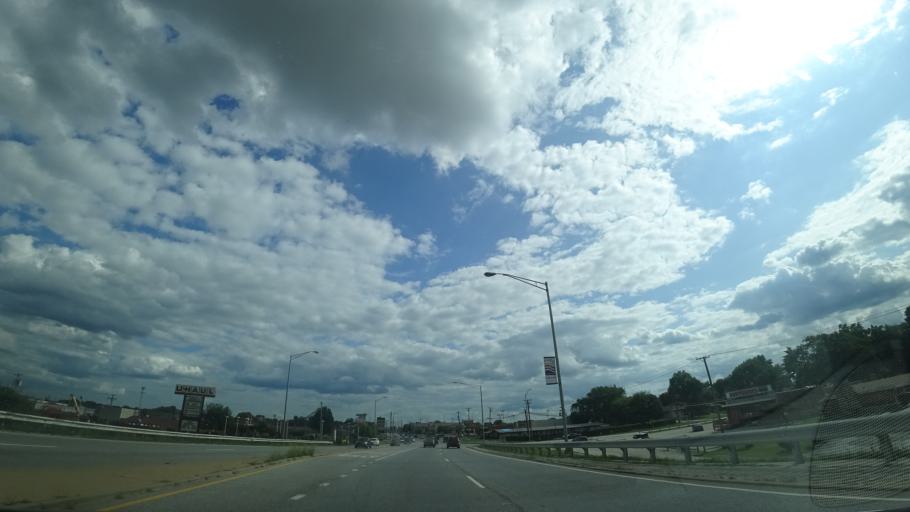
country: US
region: Illinois
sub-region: Cook County
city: Alsip
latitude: 41.6772
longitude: -87.7388
